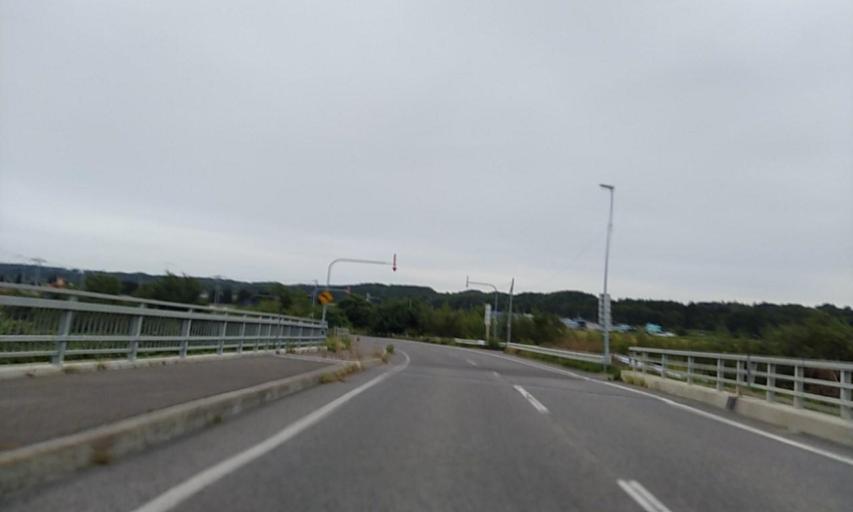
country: JP
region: Hokkaido
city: Bihoro
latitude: 43.8391
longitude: 144.1143
